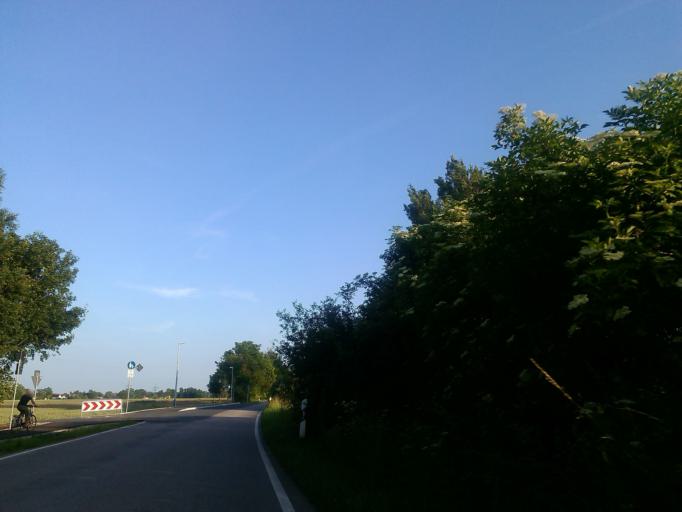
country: DE
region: Bavaria
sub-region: Upper Bavaria
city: Grobenzell
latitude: 48.1884
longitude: 11.4088
